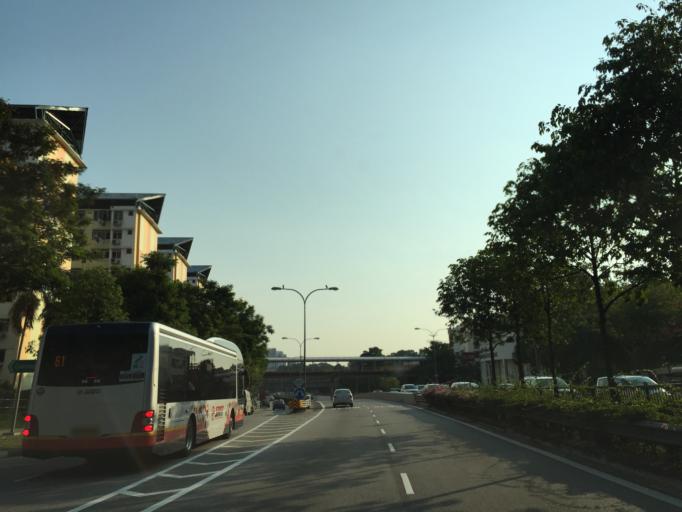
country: SG
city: Singapore
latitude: 1.2971
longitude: 103.8001
